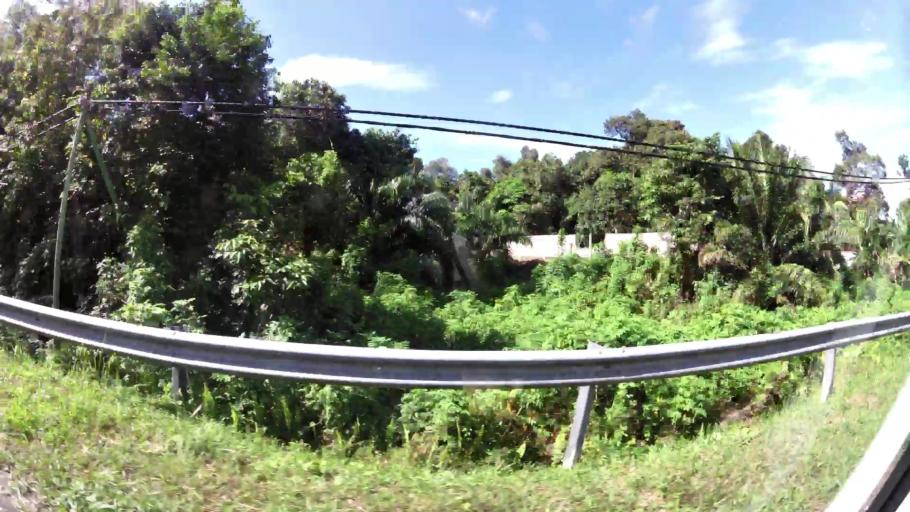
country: BN
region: Brunei and Muara
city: Bandar Seri Begawan
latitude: 4.9509
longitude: 114.9399
